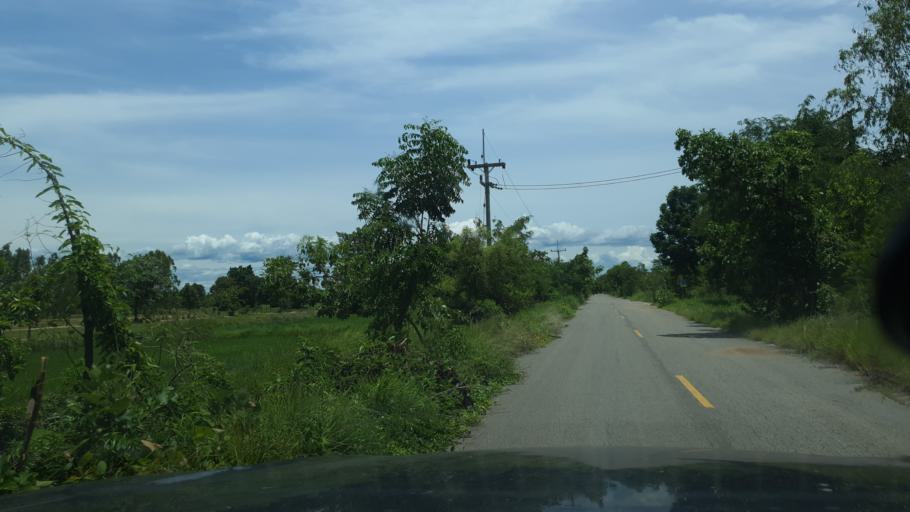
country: TH
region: Sukhothai
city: Ban Na
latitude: 17.1223
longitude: 99.6743
